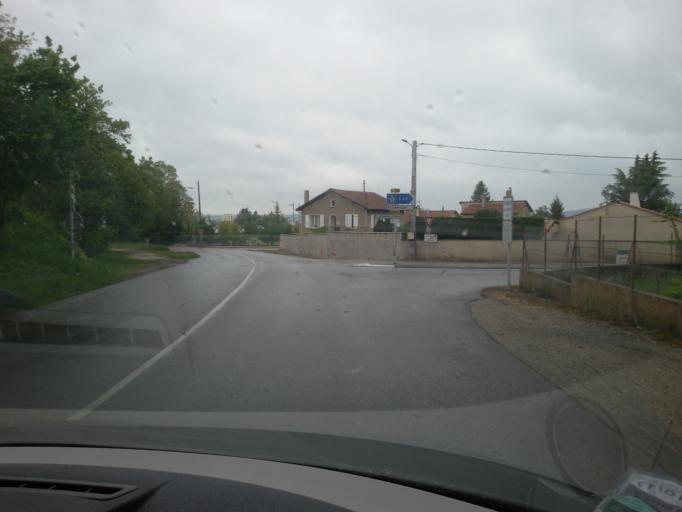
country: FR
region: Rhone-Alpes
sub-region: Departement de la Drome
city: Bourg-de-Peage
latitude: 45.0264
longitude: 5.0744
